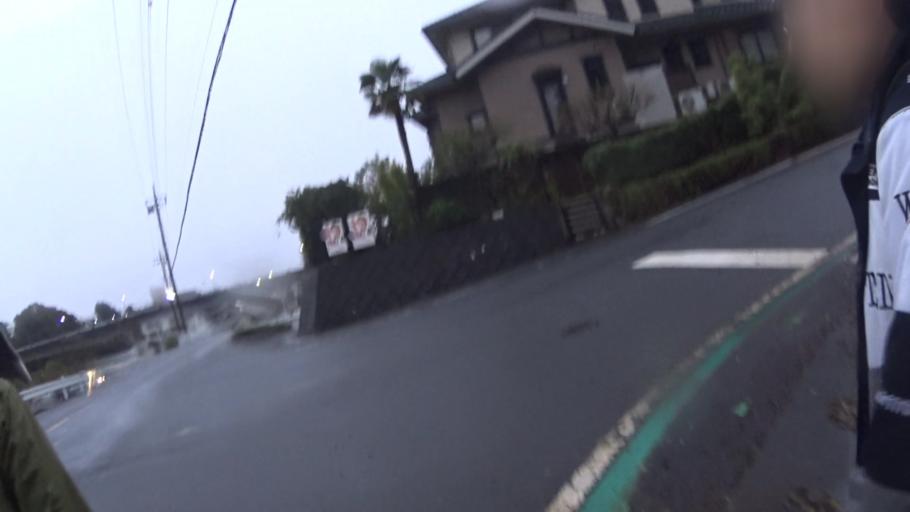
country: JP
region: Saitama
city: Hanno
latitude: 35.8485
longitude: 139.3136
